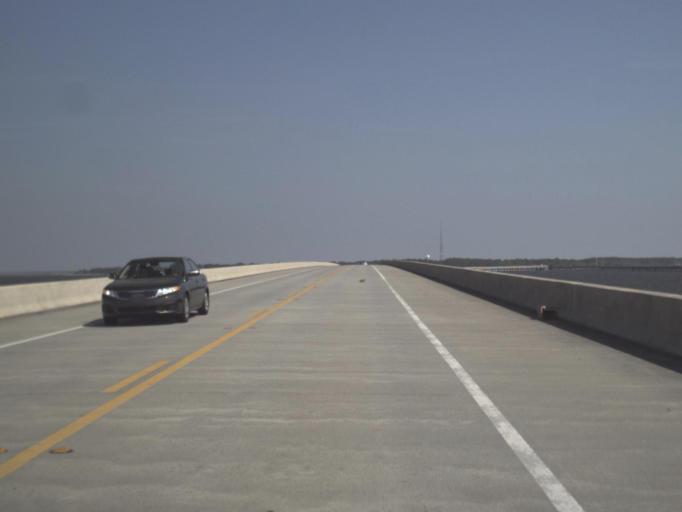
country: US
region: Florida
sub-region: Franklin County
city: Eastpoint
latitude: 29.7059
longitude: -84.8906
